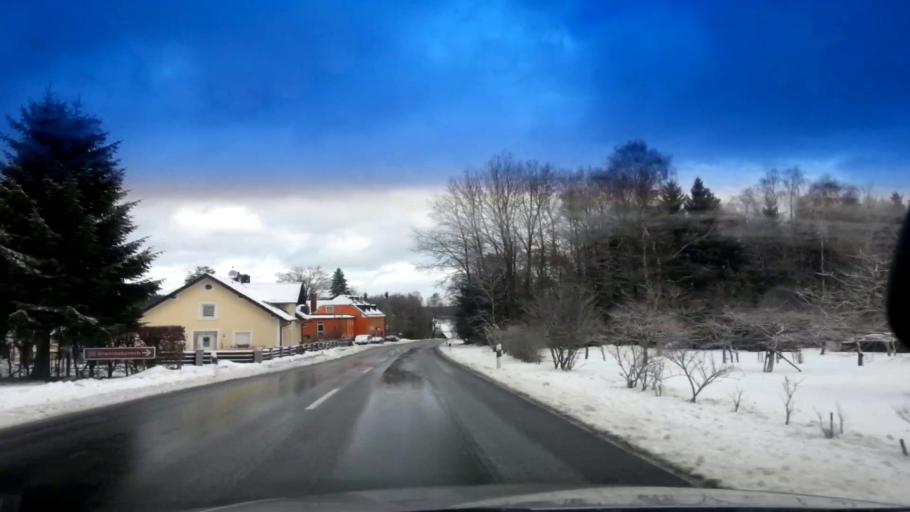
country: DE
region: Bavaria
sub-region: Upper Franconia
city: Kirchenlamitz
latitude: 50.1419
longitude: 11.9286
